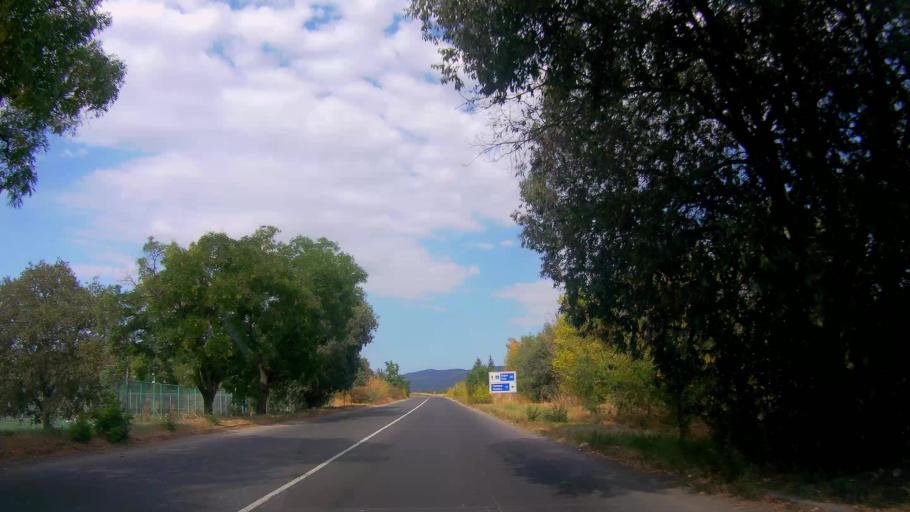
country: BG
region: Burgas
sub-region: Obshtina Aytos
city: Aytos
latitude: 42.7027
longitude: 27.2451
